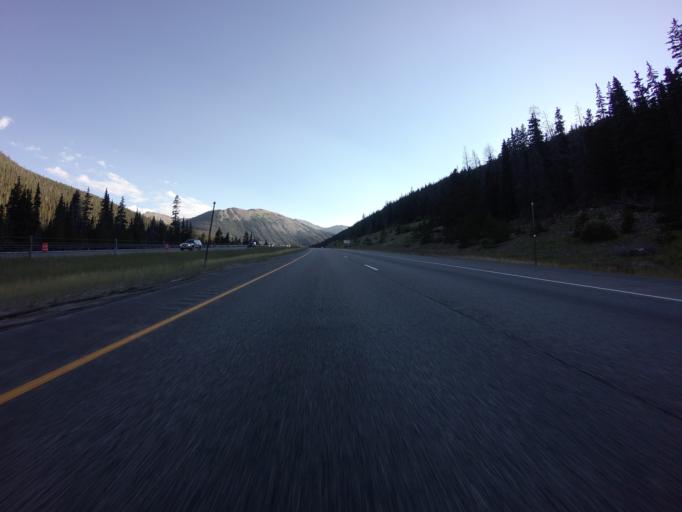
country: US
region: Colorado
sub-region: Summit County
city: Keystone
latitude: 39.6943
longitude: -105.8763
